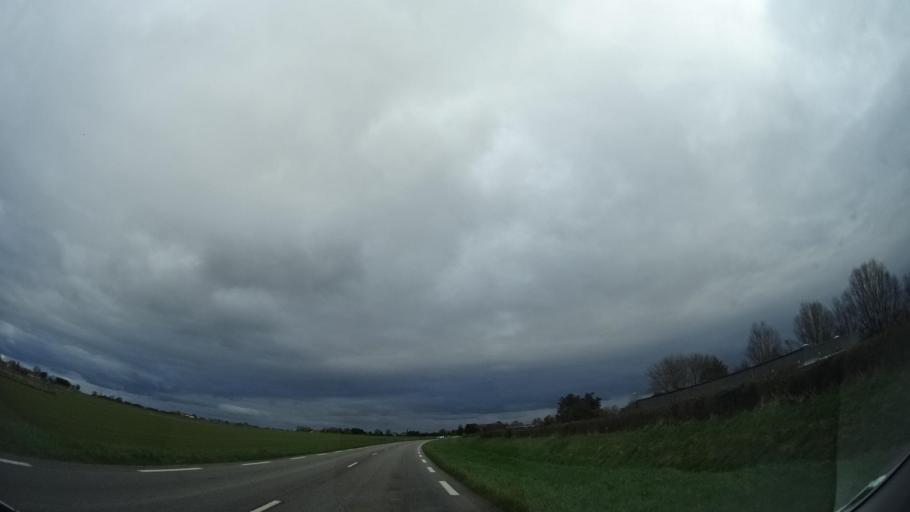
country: FR
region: Haute-Normandie
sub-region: Departement de la Seine-Maritime
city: Octeville-sur-Mer
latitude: 49.5403
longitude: 0.1018
